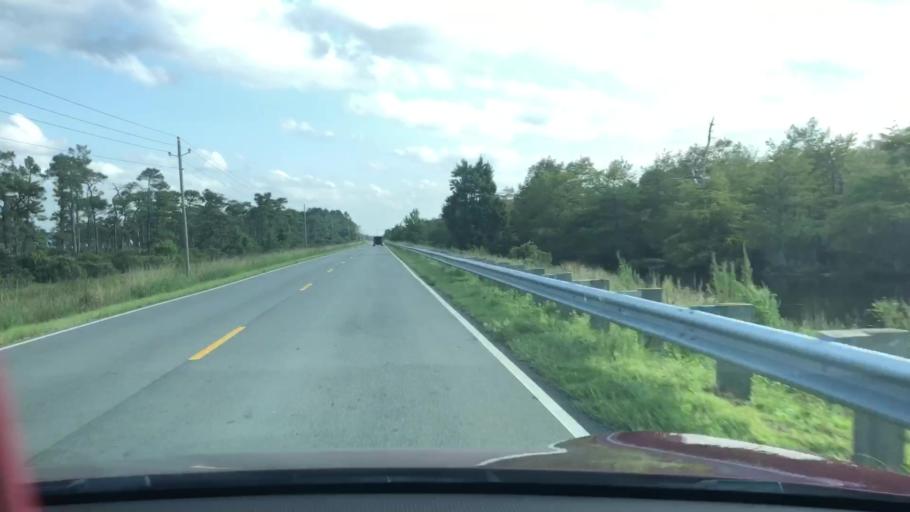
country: US
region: North Carolina
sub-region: Dare County
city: Wanchese
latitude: 35.7740
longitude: -75.7693
